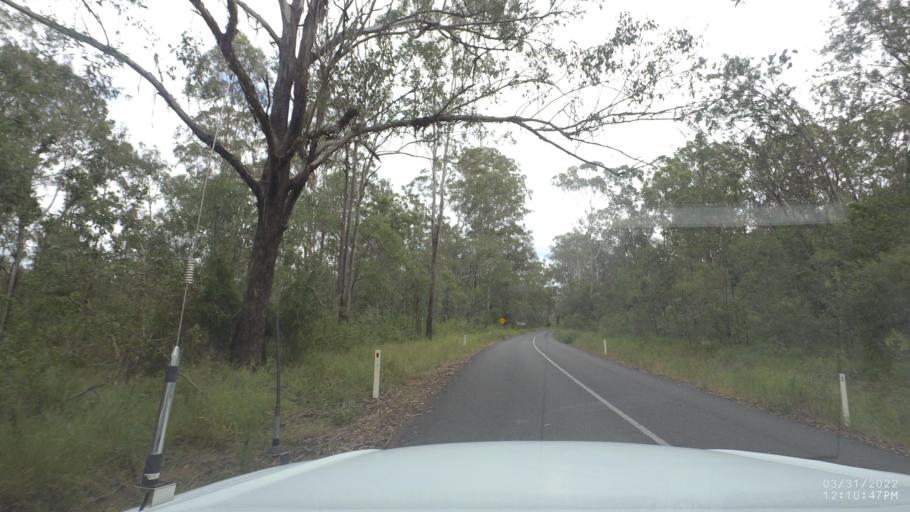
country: AU
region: Queensland
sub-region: Logan
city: Cedar Vale
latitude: -27.9327
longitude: 153.0783
